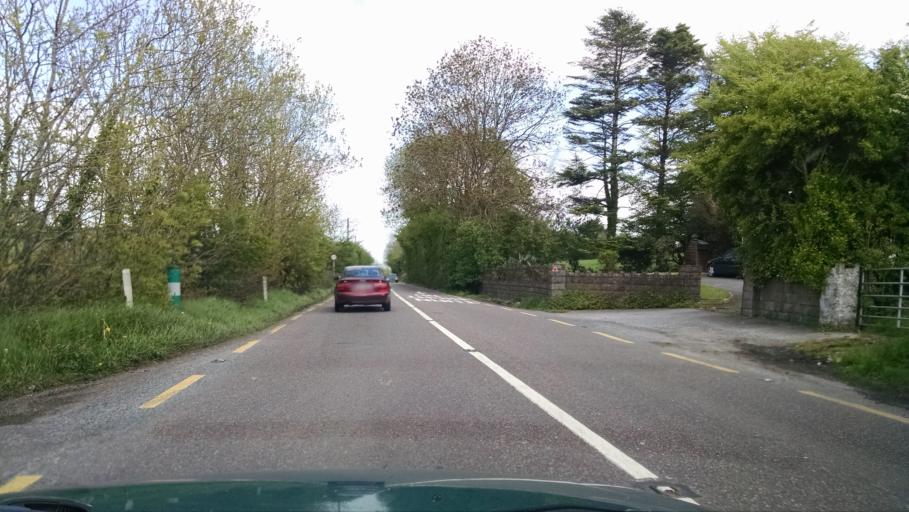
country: IE
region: Munster
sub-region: County Cork
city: Carrigaline
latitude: 51.8523
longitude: -8.4182
